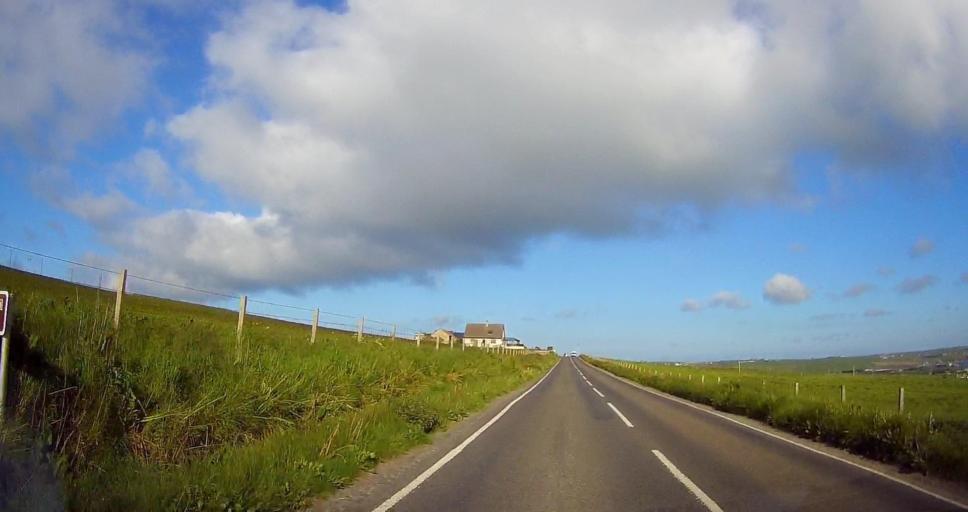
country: GB
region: Scotland
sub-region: Orkney Islands
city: Orkney
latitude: 58.9781
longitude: -3.0115
